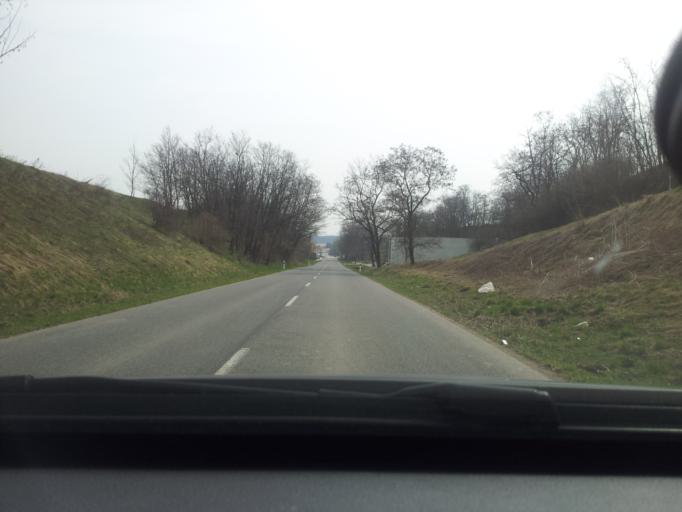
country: SK
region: Trnavsky
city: Leopoldov
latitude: 48.4604
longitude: 17.7102
